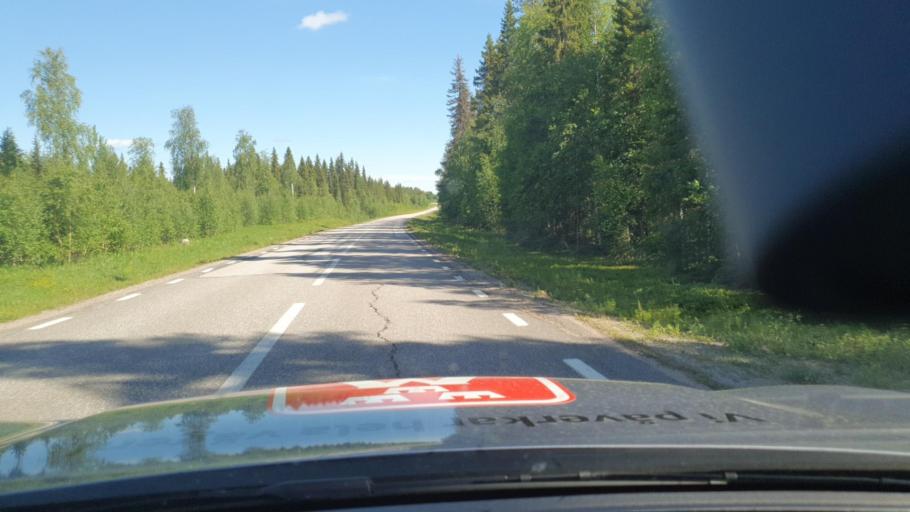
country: SE
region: Norrbotten
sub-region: Overkalix Kommun
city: OEverkalix
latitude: 66.7561
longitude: 22.6746
